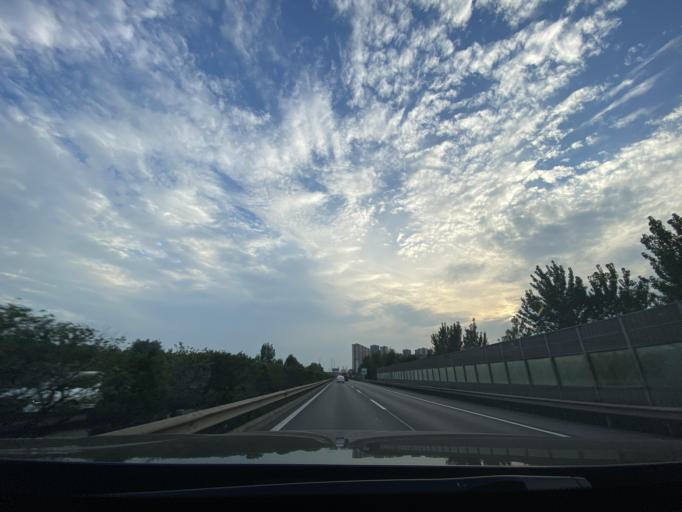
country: CN
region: Sichuan
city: Deyang
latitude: 31.0825
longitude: 104.3938
